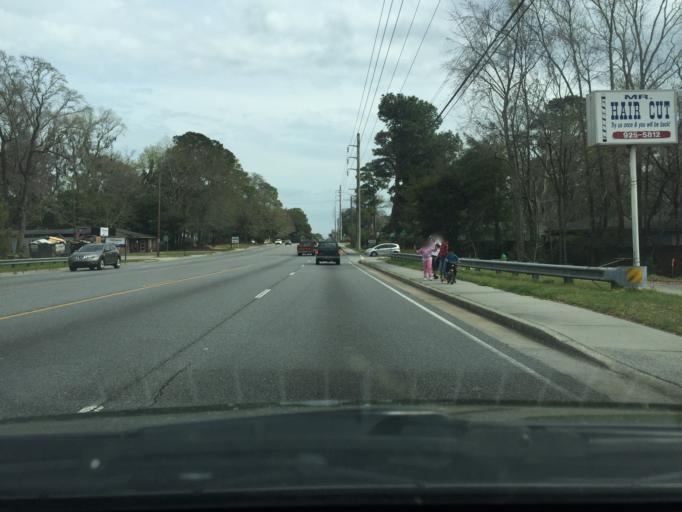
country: US
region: Georgia
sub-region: Chatham County
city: Isle of Hope
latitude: 31.9953
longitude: -81.1110
